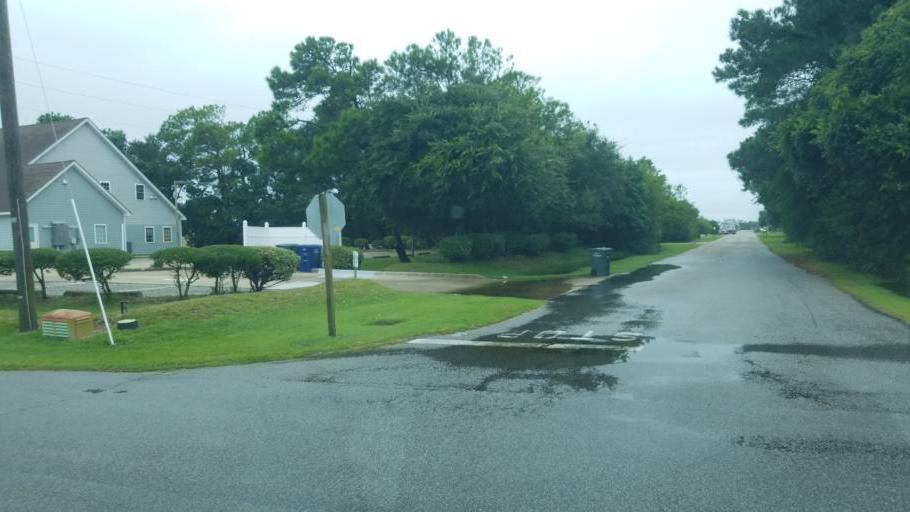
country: US
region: North Carolina
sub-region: Dare County
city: Nags Head
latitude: 35.9893
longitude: -75.6452
